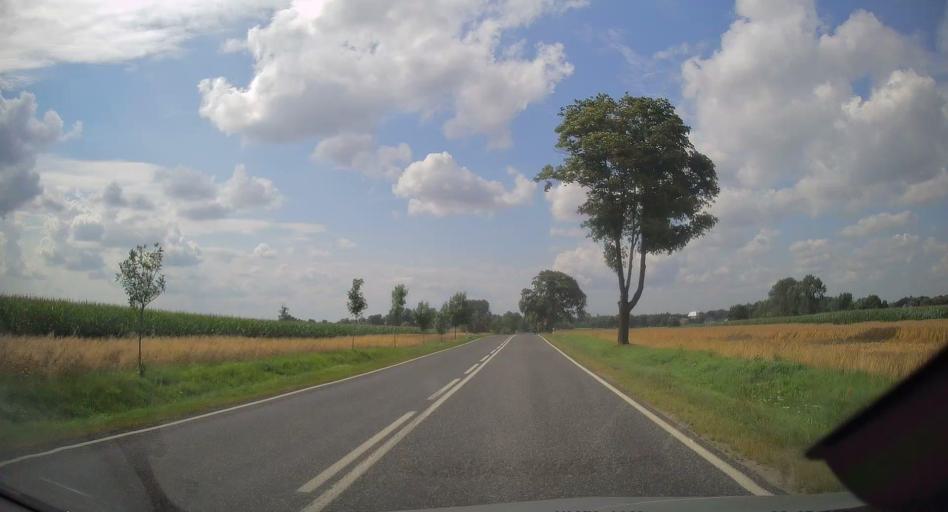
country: PL
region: Lodz Voivodeship
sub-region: Powiat brzezinski
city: Jezow
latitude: 51.8012
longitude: 20.0206
